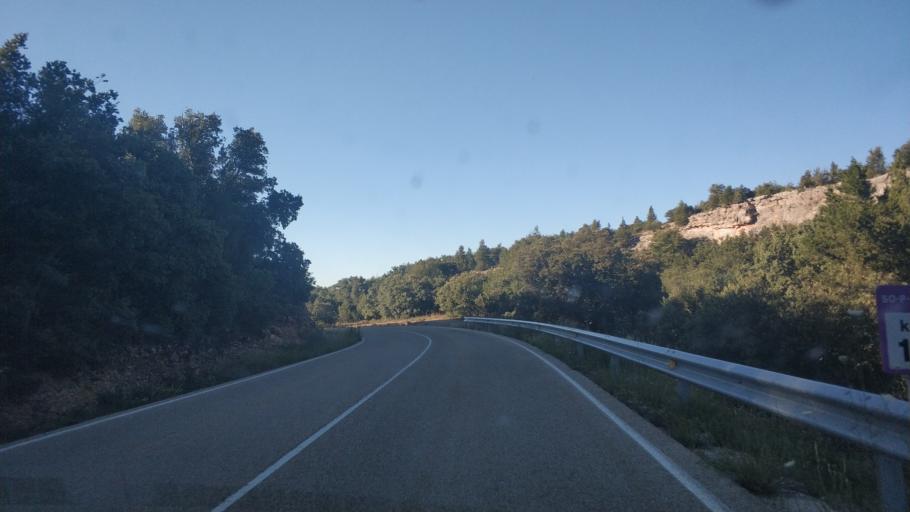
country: ES
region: Castille and Leon
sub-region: Provincia de Soria
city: Montejo de Tiermes
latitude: 41.4203
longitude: -3.2050
